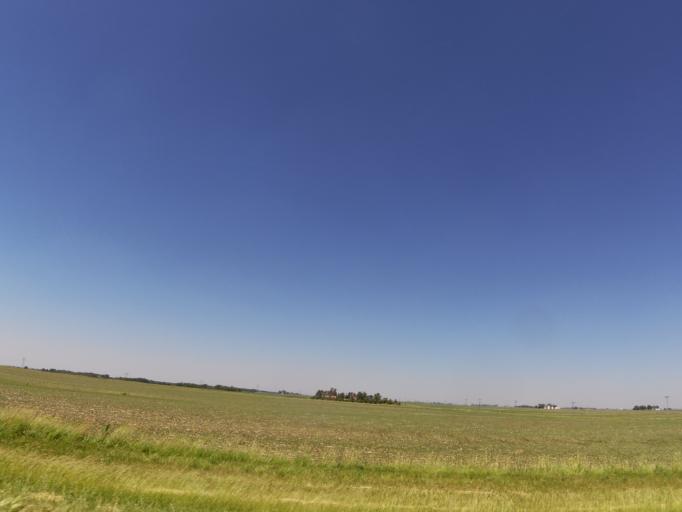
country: US
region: Illinois
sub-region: McLean County
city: Chenoa
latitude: 40.7423
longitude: -88.6623
